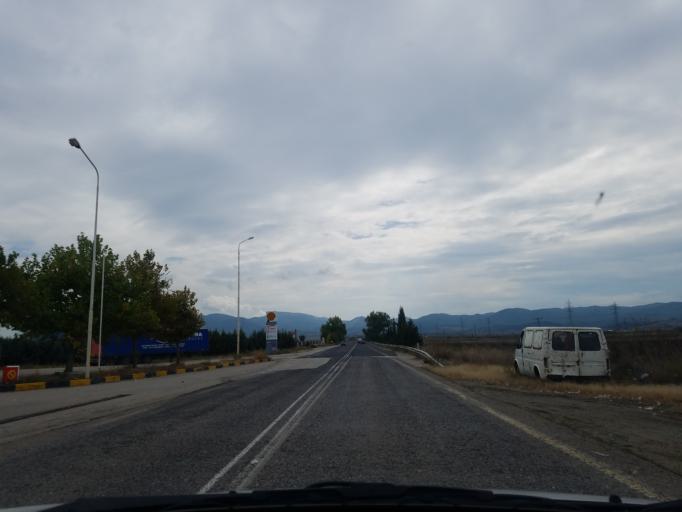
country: GR
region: Central Greece
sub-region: Nomos Fthiotidos
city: Omvriaki
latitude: 39.0757
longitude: 22.3170
